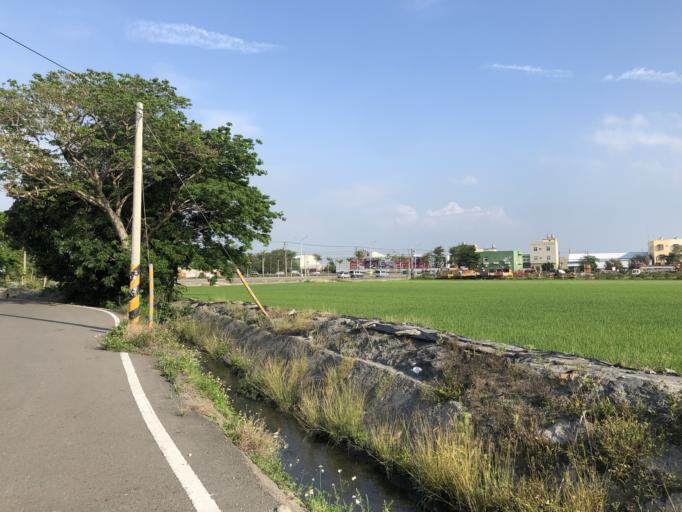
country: TW
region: Taiwan
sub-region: Changhua
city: Chang-hua
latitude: 24.0500
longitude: 120.4681
